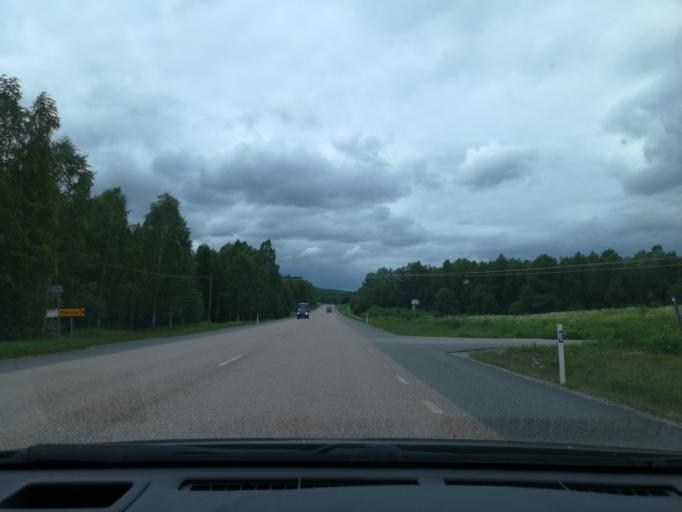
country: SE
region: Vaestmanland
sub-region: Fagersta Kommun
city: Fagersta
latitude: 59.9793
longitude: 15.6945
